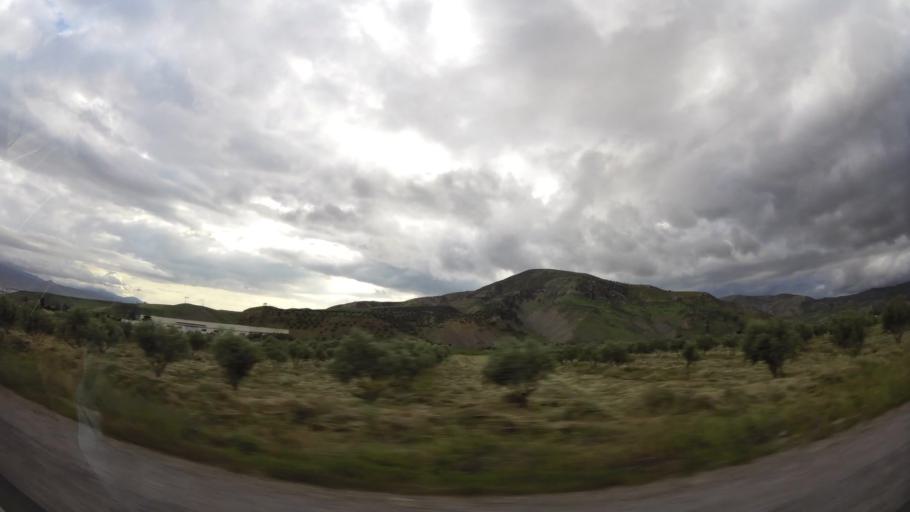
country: MA
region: Taza-Al Hoceima-Taounate
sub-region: Taza
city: Taza
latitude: 34.2750
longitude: -3.9562
